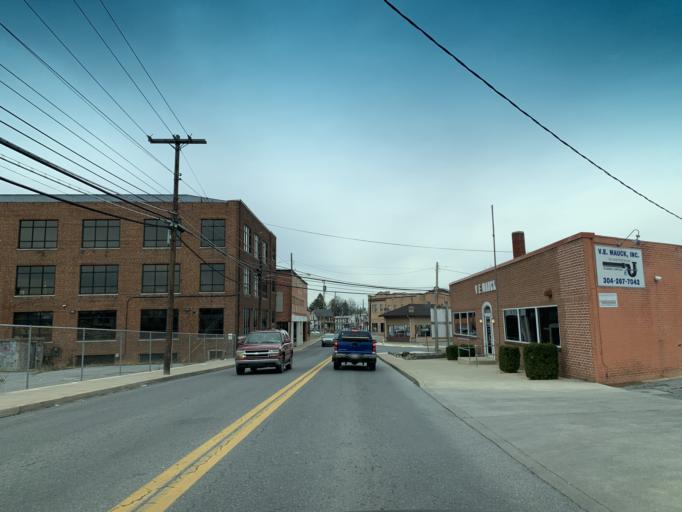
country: US
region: West Virginia
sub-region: Berkeley County
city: Martinsburg
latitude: 39.4558
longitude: -77.9717
